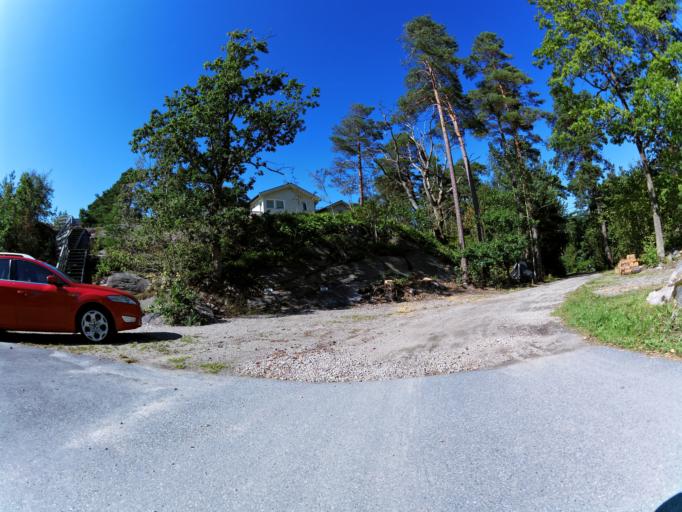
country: NO
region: Ostfold
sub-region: Fredrikstad
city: Fredrikstad
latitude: 59.1742
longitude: 10.8539
